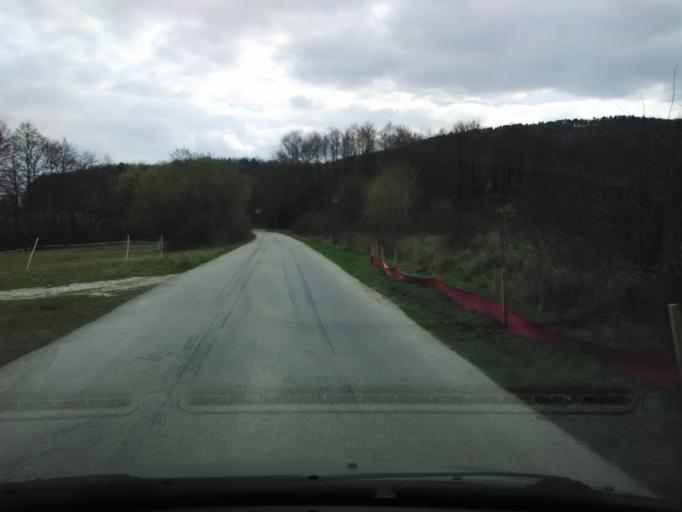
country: SK
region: Nitriansky
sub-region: Okres Nitra
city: Nitra
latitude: 48.3949
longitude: 18.2075
